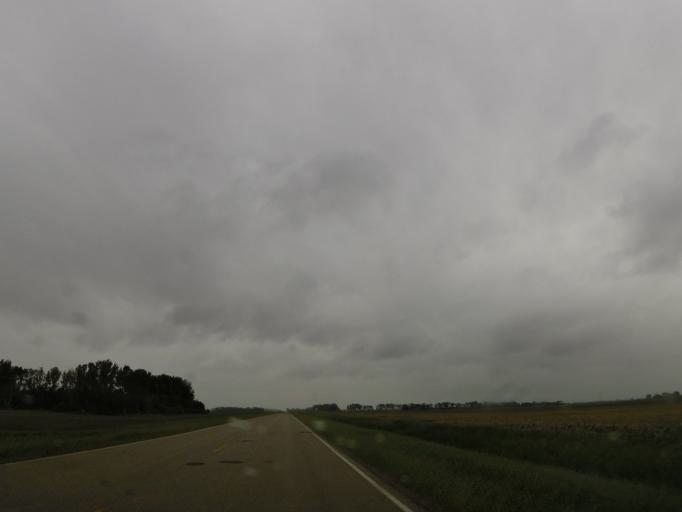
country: US
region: North Dakota
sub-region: Walsh County
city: Grafton
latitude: 48.5686
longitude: -97.2997
